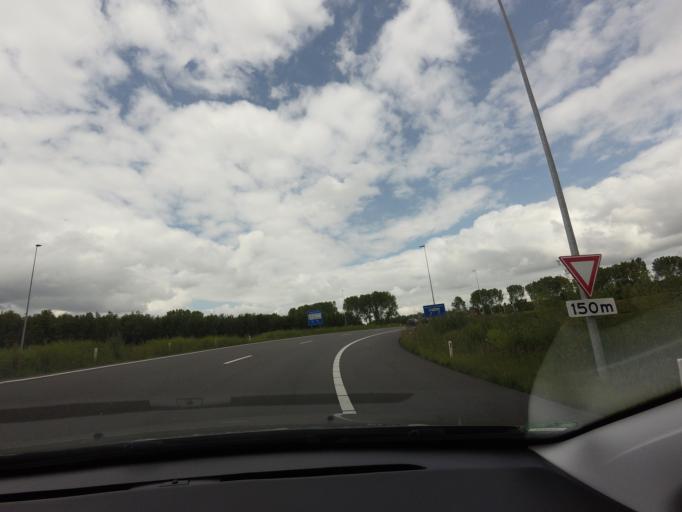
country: NL
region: Flevoland
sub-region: Gemeente Almere
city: Almere Stad
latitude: 52.3733
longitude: 5.2856
